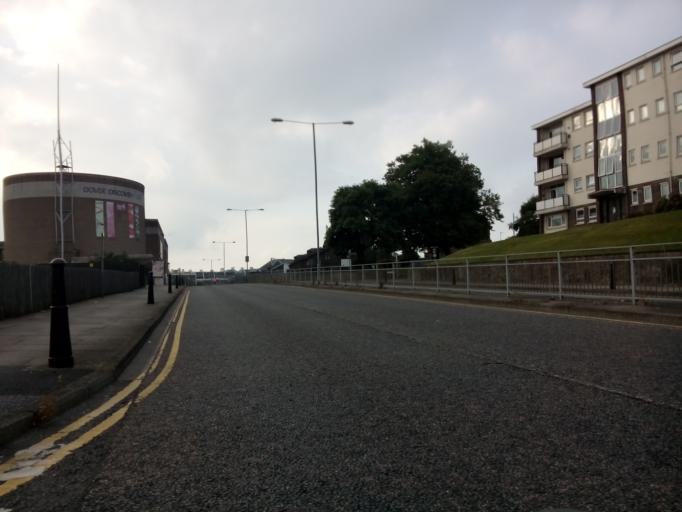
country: GB
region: England
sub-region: Kent
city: Dover
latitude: 51.1255
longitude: 1.3112
